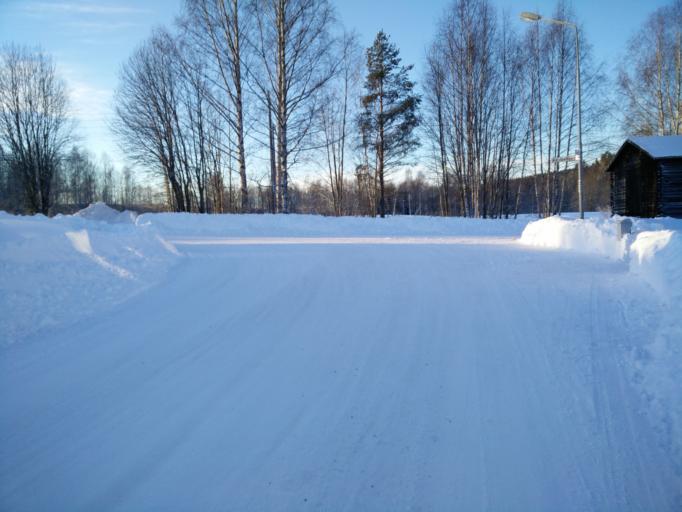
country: SE
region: Vaesternorrland
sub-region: Sundsvalls Kommun
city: Nolby
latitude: 62.2954
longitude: 17.3598
